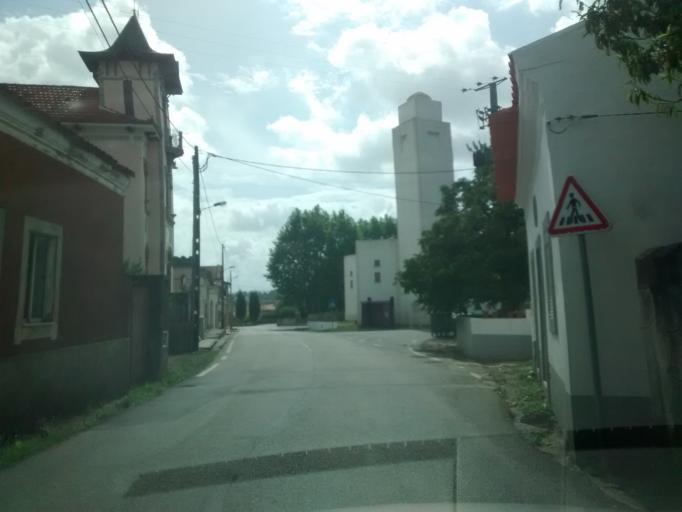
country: PT
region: Aveiro
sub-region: Anadia
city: Sangalhos
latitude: 40.4824
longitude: -8.4885
